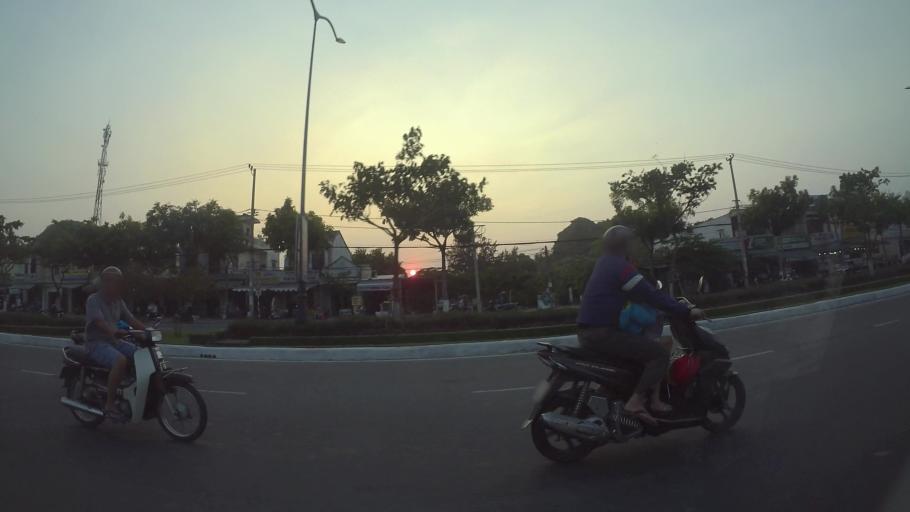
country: VN
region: Da Nang
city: Ngu Hanh Son
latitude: 16.0037
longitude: 108.2597
